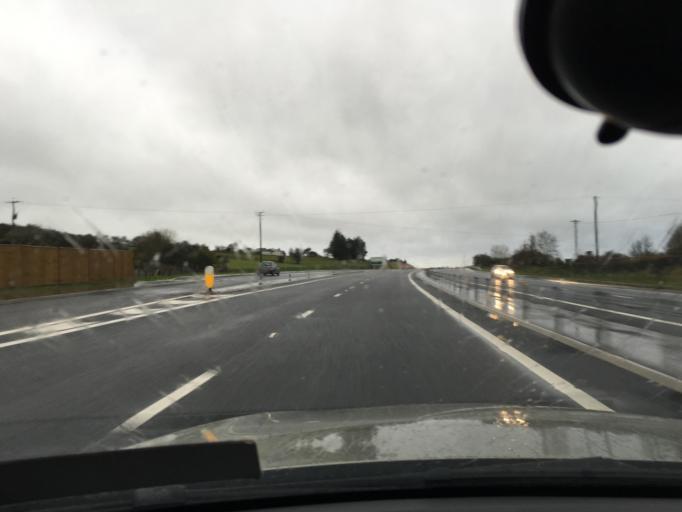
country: GB
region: Northern Ireland
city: Ballyclare
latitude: 54.7975
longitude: -5.9283
